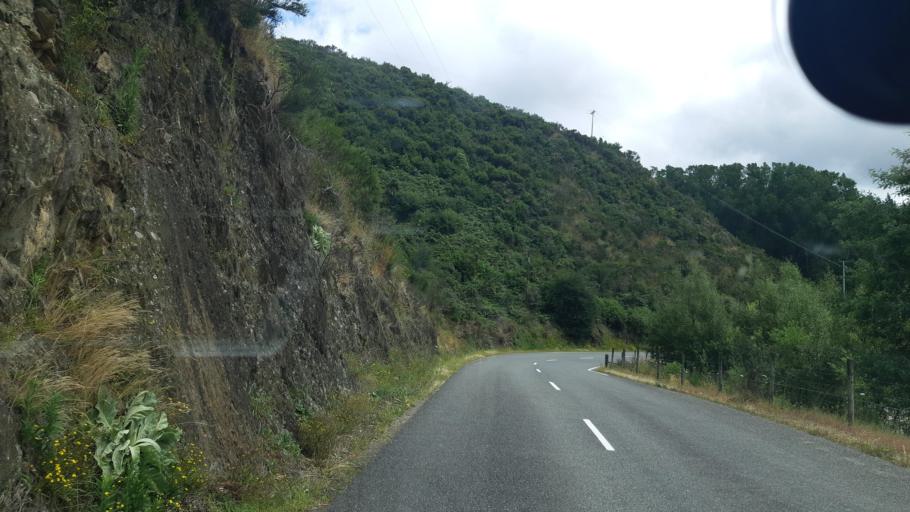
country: NZ
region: Marlborough
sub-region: Marlborough District
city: Blenheim
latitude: -41.4853
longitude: 173.7453
